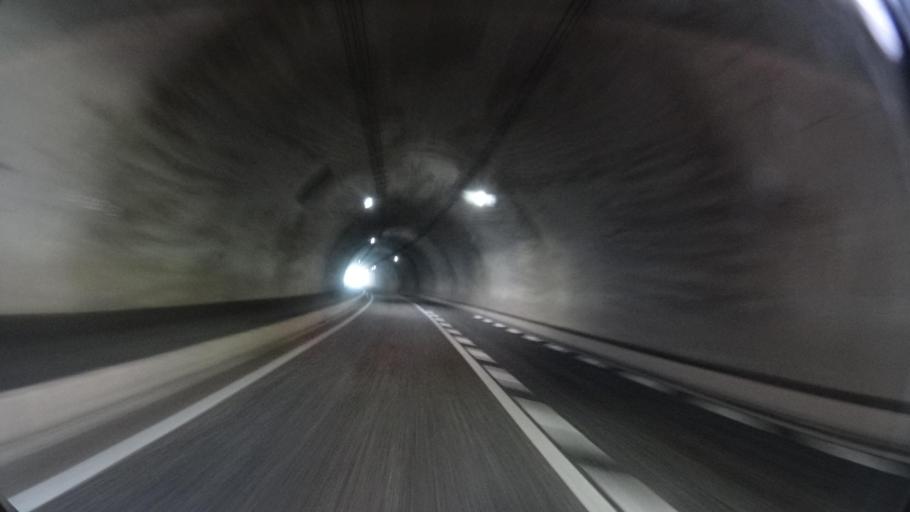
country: JP
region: Kyoto
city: Maizuru
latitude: 35.5350
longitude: 135.3476
